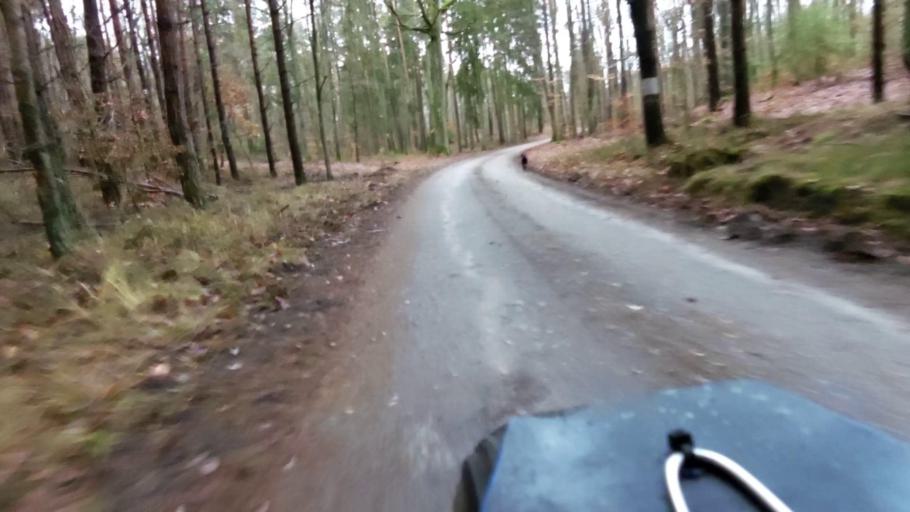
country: PL
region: Lubusz
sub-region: Powiat gorzowski
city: Bogdaniec
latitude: 52.6932
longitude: 15.0047
